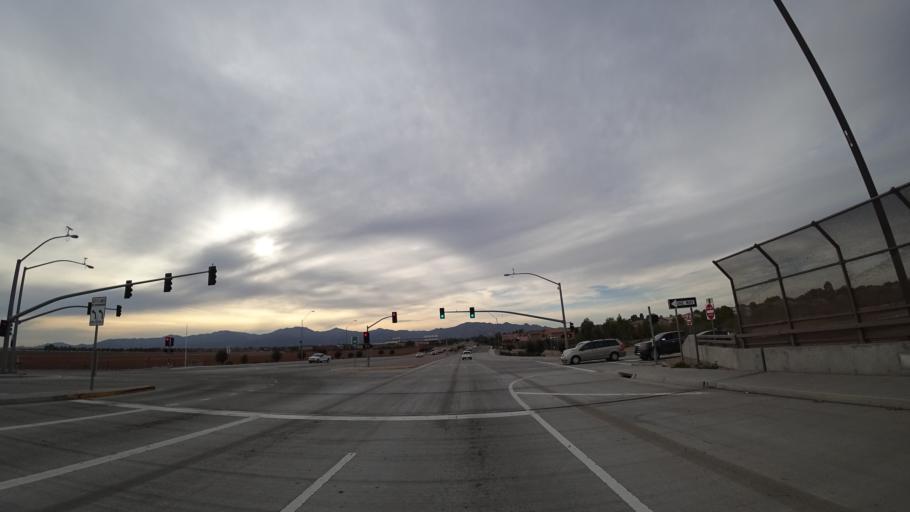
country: US
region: Arizona
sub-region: Maricopa County
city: Citrus Park
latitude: 33.6241
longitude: -112.4182
